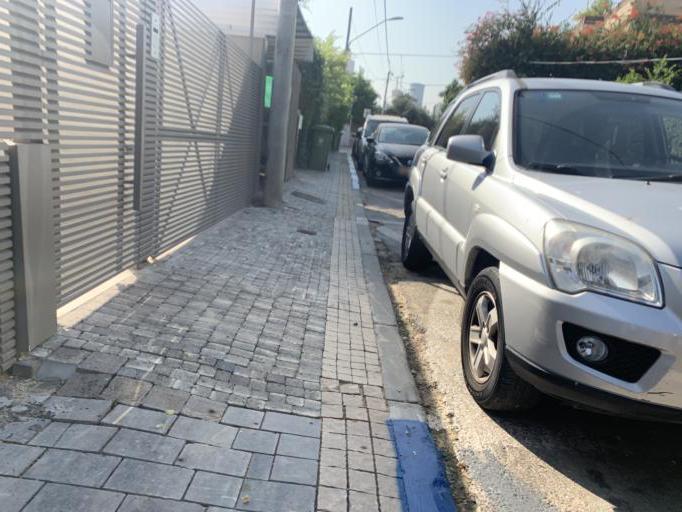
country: IL
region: Tel Aviv
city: Ramat Gan
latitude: 32.0921
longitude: 34.8141
